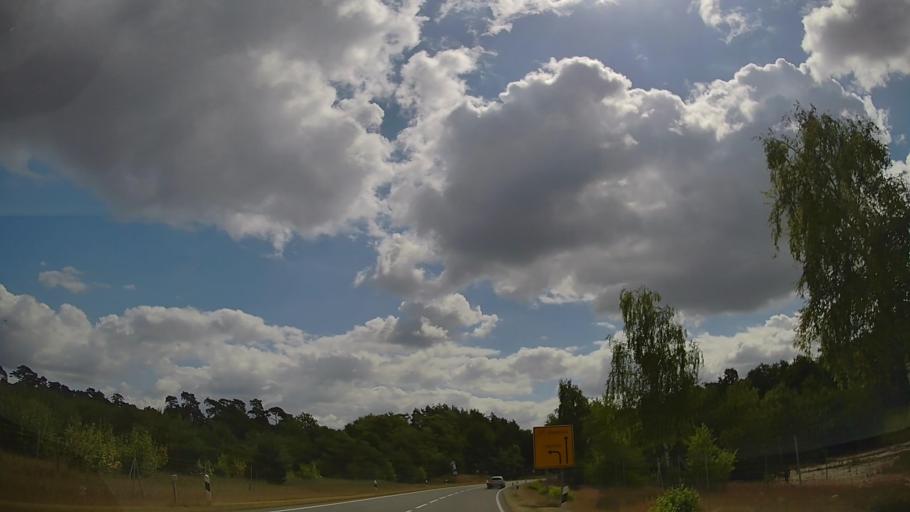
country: DE
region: Lower Saxony
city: Vechta
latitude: 52.7023
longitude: 8.2958
